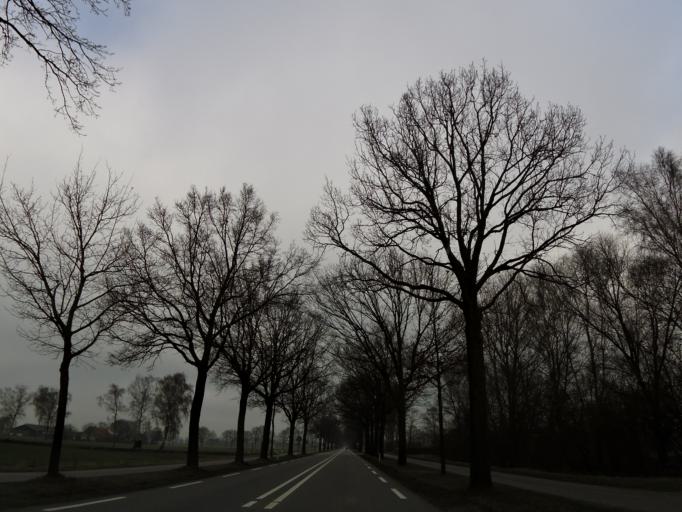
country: NL
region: North Brabant
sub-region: Gemeente Mill en Sint Hubert
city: Wilbertoord
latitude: 51.5956
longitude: 5.7582
